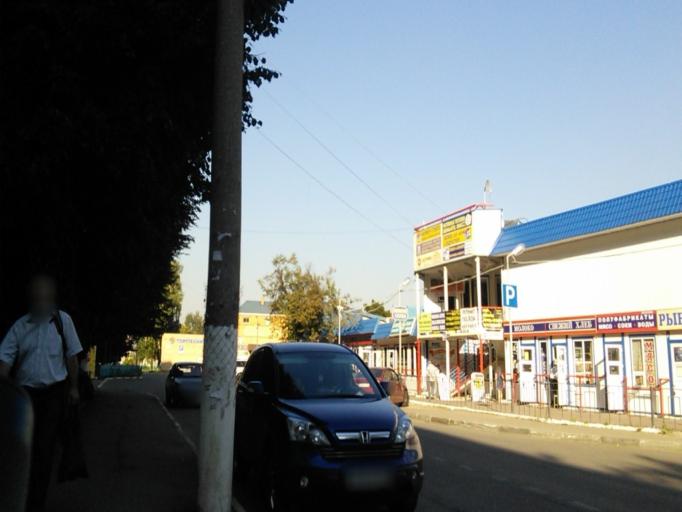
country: RU
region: Moskovskaya
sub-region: Podol'skiy Rayon
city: Podol'sk
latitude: 55.4377
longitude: 37.5652
